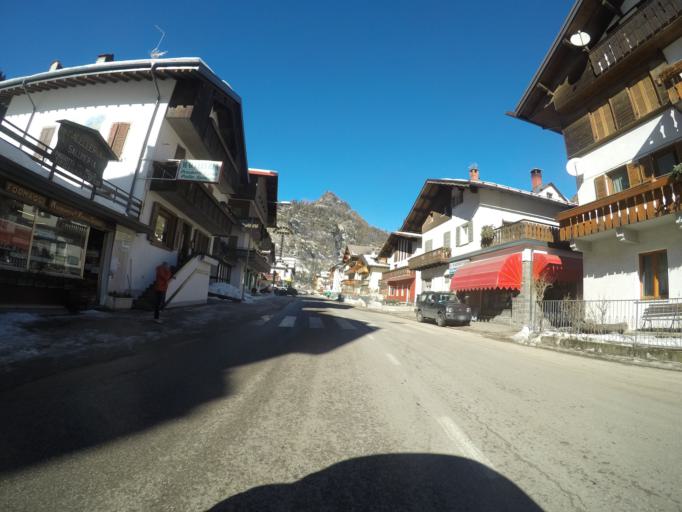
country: IT
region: Veneto
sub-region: Provincia di Belluno
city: Rocca Pietore
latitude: 46.4380
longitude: 11.9948
